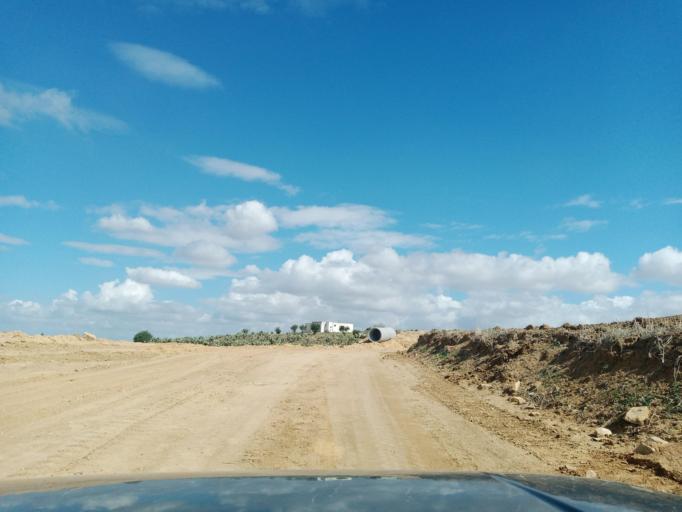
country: TN
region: Tunis
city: Oued Lill
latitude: 36.8159
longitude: 9.9996
